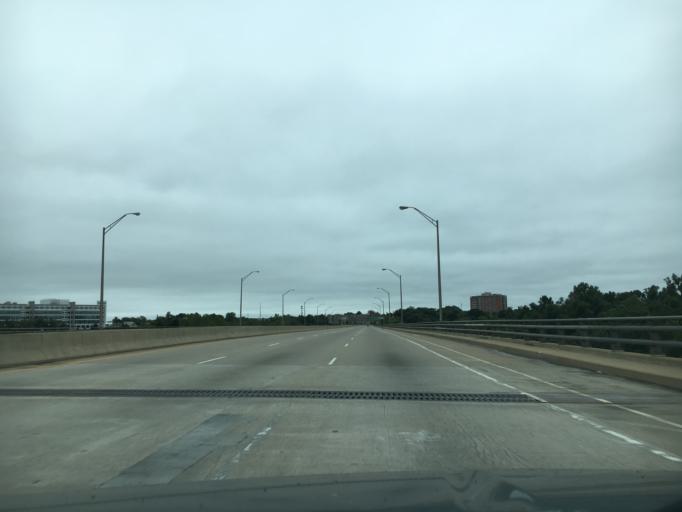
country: US
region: Virginia
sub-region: City of Richmond
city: Richmond
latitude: 37.5321
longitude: -77.4499
